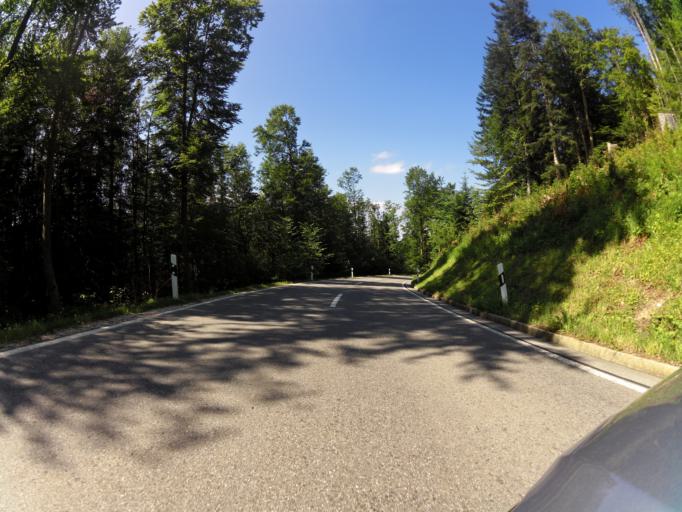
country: DE
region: Bavaria
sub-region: Upper Bavaria
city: Berchtesgaden
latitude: 47.6318
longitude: 13.0393
